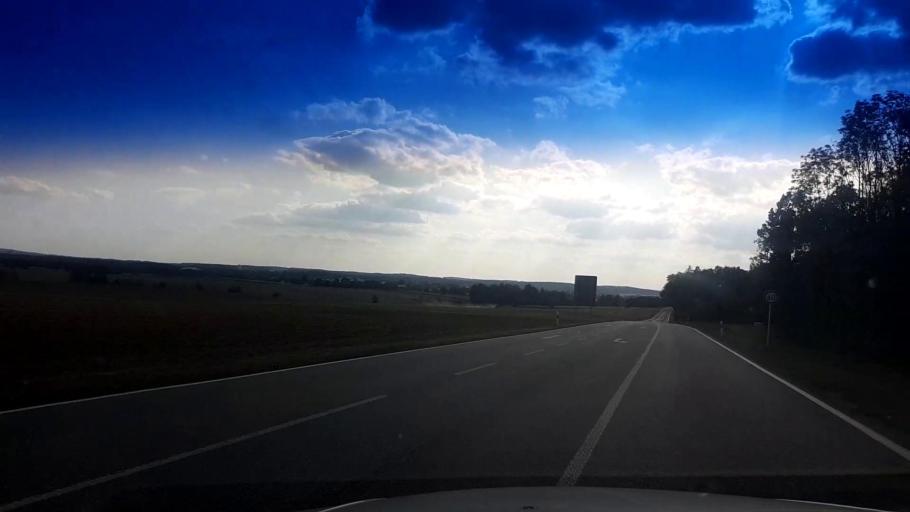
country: DE
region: Bavaria
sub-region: Upper Palatinate
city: Tirschenreuth
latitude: 49.8869
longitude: 12.3682
